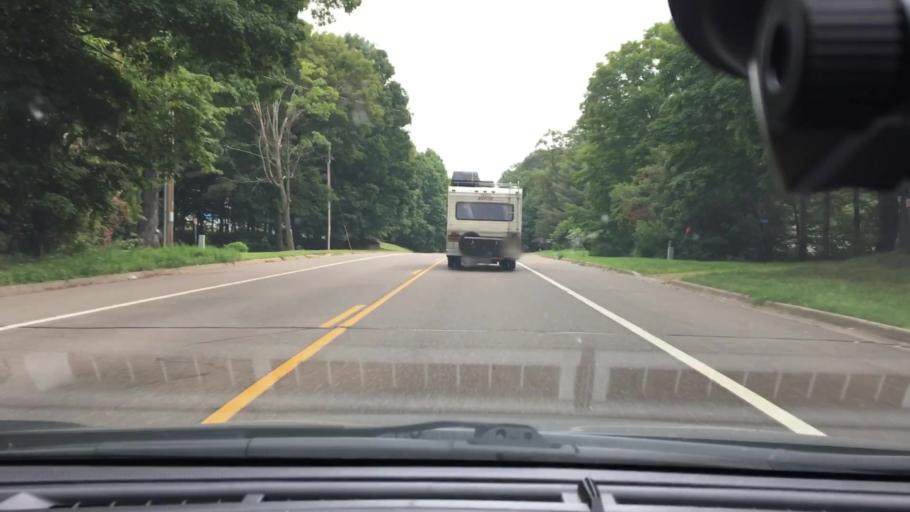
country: US
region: Minnesota
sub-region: Crow Wing County
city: Crosby
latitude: 46.4103
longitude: -93.8630
